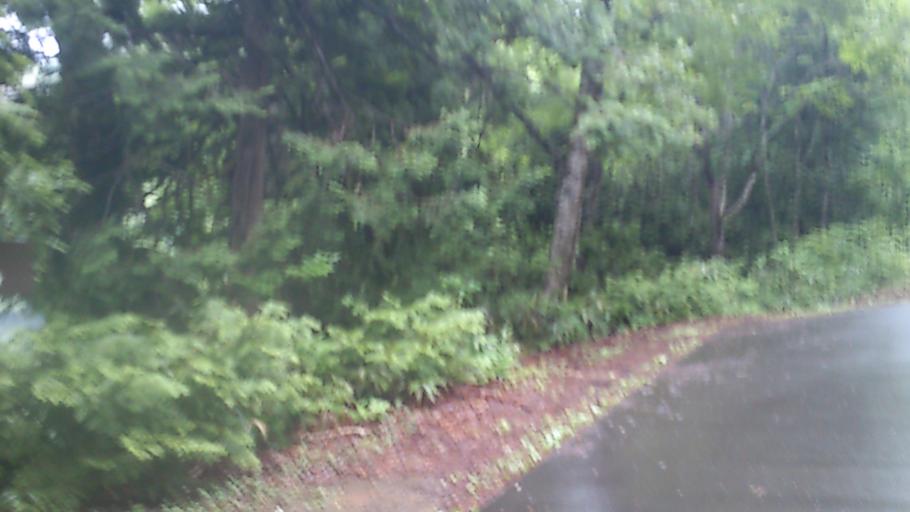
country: JP
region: Akita
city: Noshiromachi
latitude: 40.5663
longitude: 139.9753
